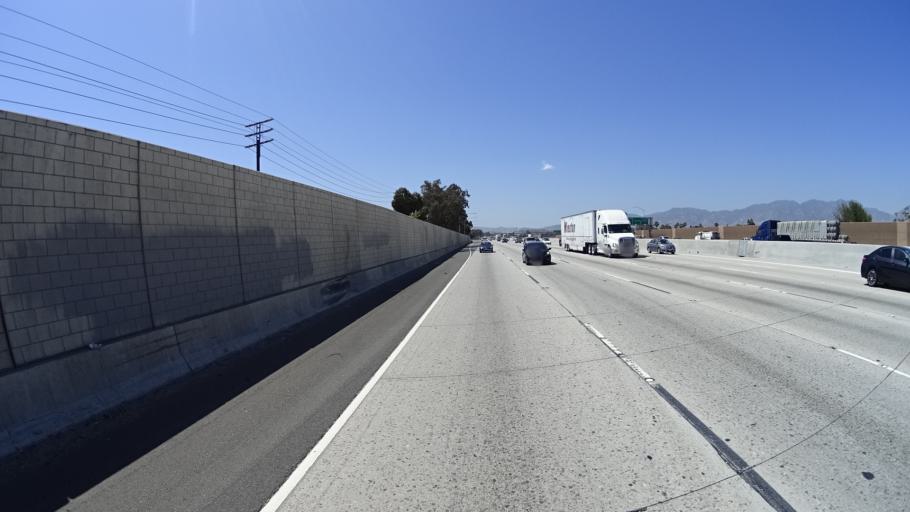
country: US
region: California
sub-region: Los Angeles County
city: San Fernando
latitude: 34.2522
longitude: -118.4307
